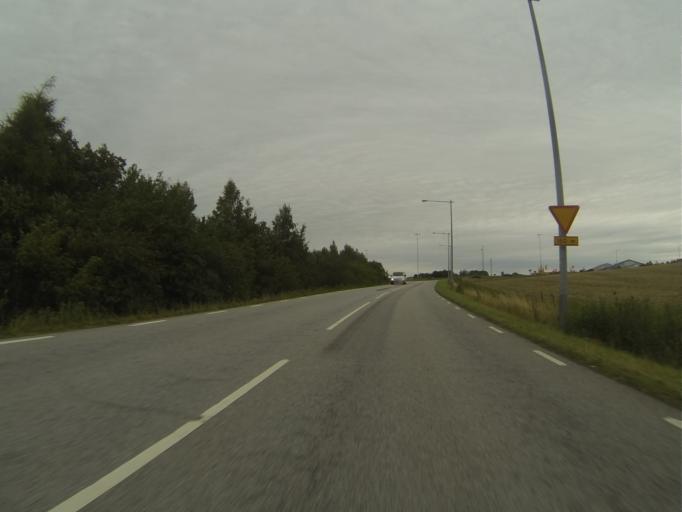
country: SE
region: Skane
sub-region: Staffanstorps Kommun
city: Staffanstorp
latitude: 55.6259
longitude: 13.1862
